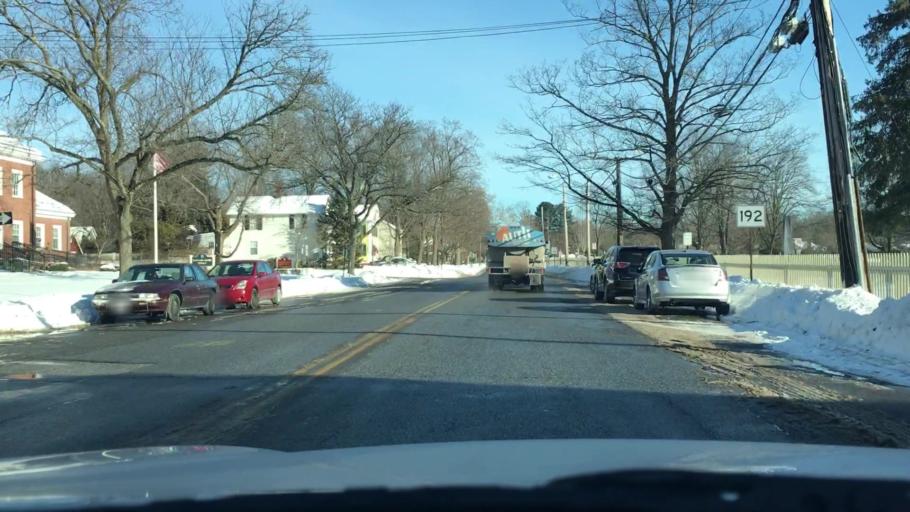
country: US
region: Massachusetts
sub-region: Hampden County
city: Longmeadow
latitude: 42.0503
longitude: -72.5812
